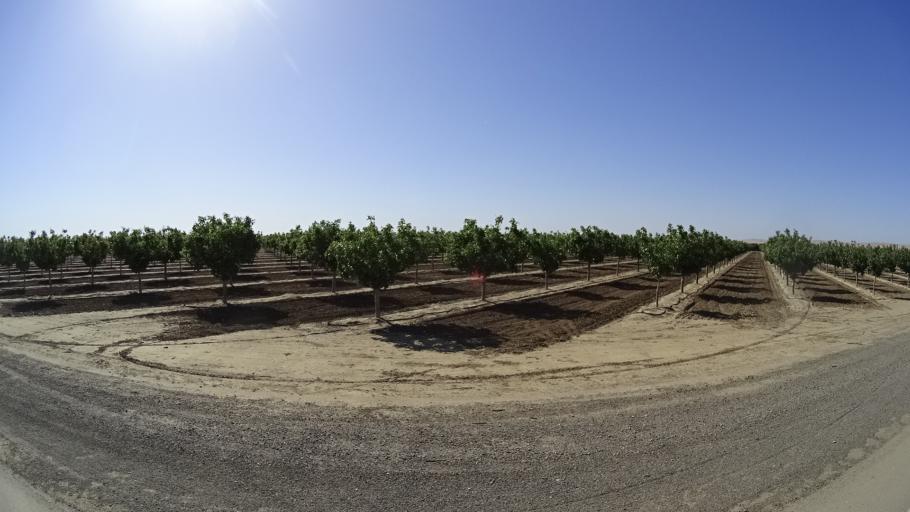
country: US
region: California
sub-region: Fresno County
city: Huron
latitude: 36.1254
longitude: -120.0271
